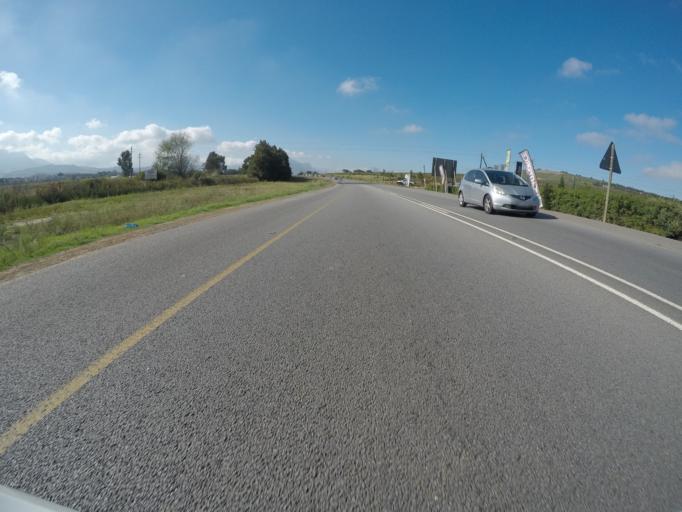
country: ZA
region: Western Cape
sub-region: Cape Winelands District Municipality
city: Stellenbosch
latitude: -33.8773
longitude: 18.8146
